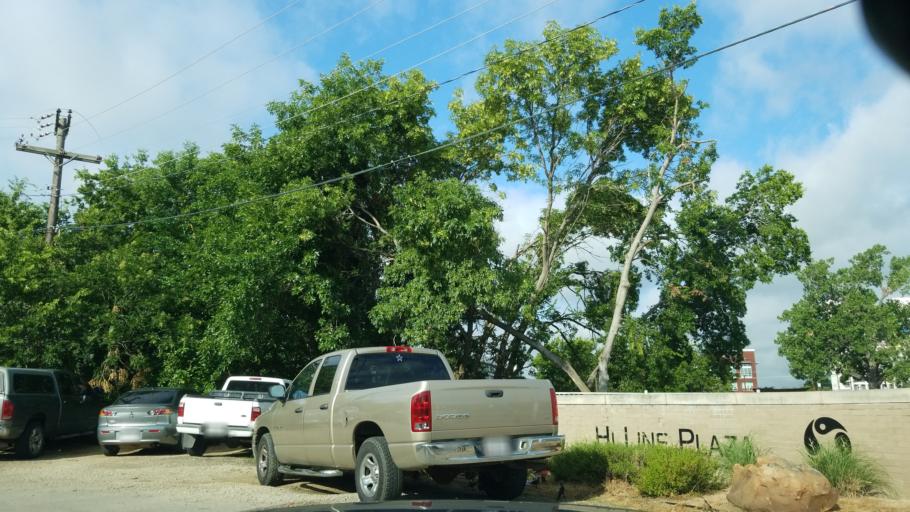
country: US
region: Texas
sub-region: Dallas County
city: Dallas
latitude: 32.7980
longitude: -96.8230
